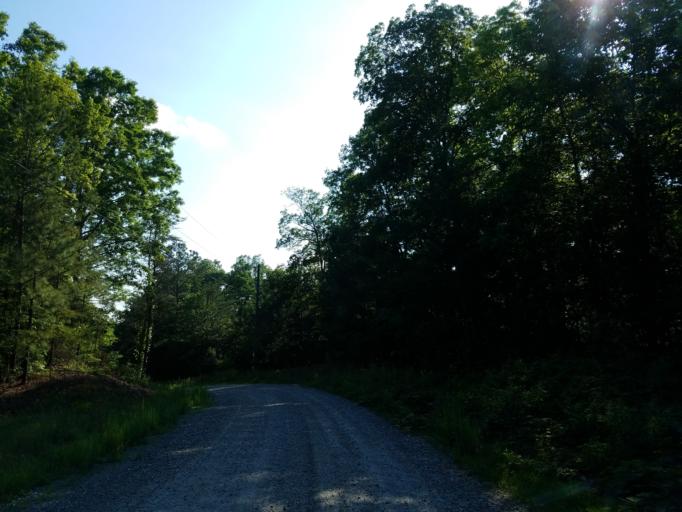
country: US
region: Georgia
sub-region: Pickens County
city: Nelson
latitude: 34.3674
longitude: -84.3447
